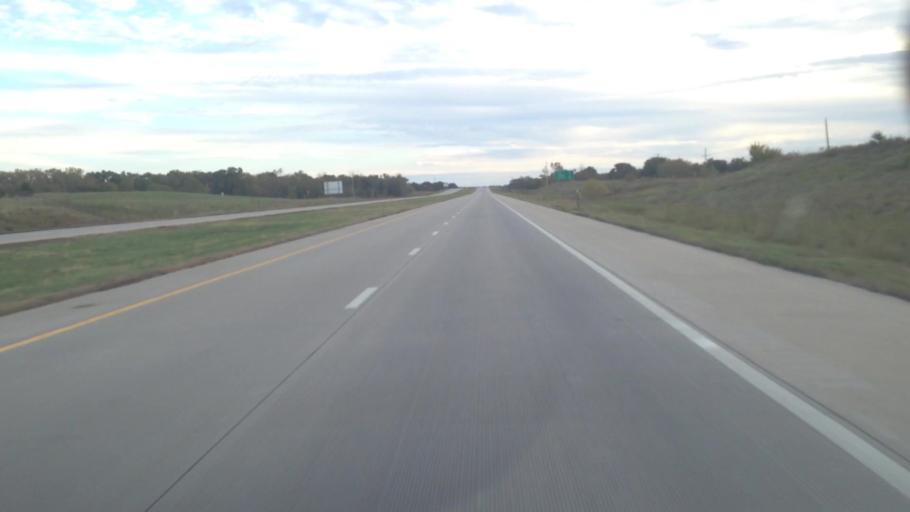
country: US
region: Kansas
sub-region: Douglas County
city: Baldwin City
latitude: 38.7716
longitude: -95.2688
